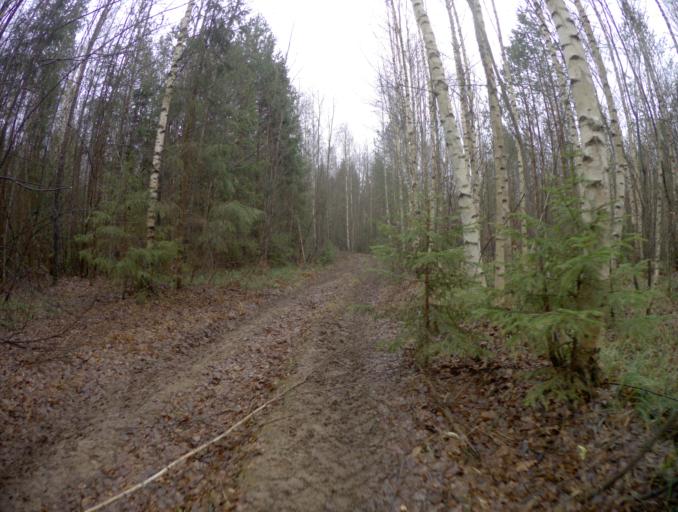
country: RU
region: Vladimir
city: Golovino
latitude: 56.0018
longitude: 40.4708
